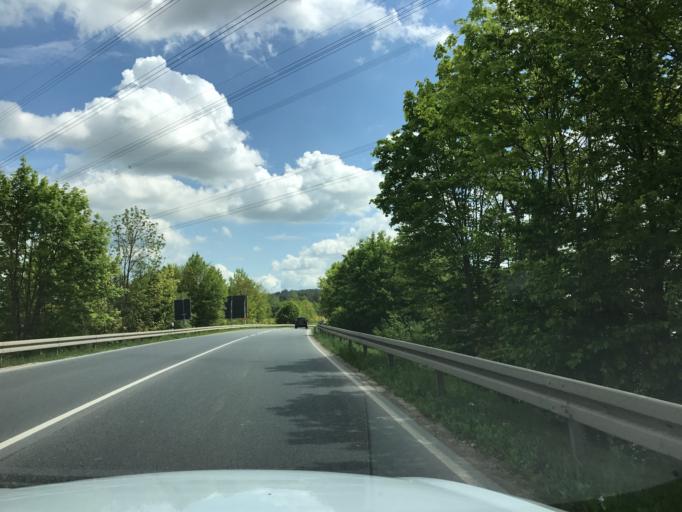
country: DE
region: Bavaria
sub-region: Upper Franconia
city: Forchheim
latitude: 49.6986
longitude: 11.0700
